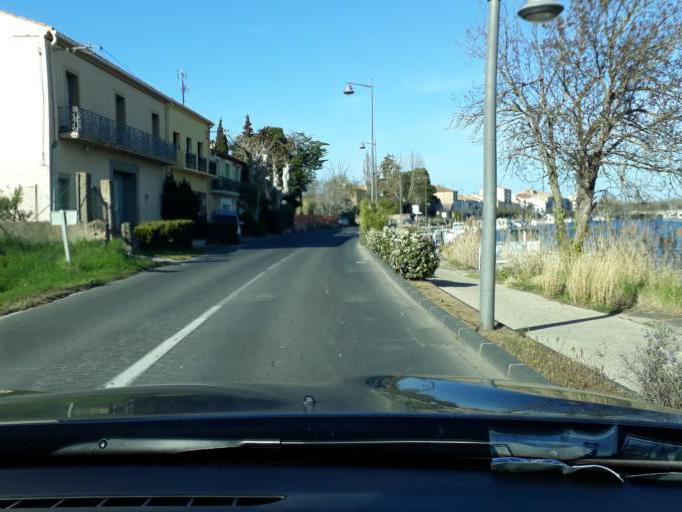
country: FR
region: Languedoc-Roussillon
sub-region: Departement de l'Herault
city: Agde
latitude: 43.3099
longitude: 3.4640
